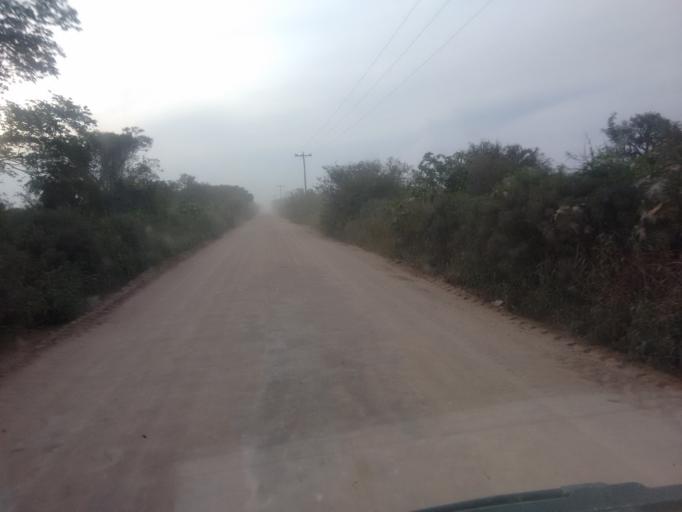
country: BR
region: Rio Grande do Sul
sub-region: Camaqua
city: Camaqua
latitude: -30.9250
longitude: -51.7958
